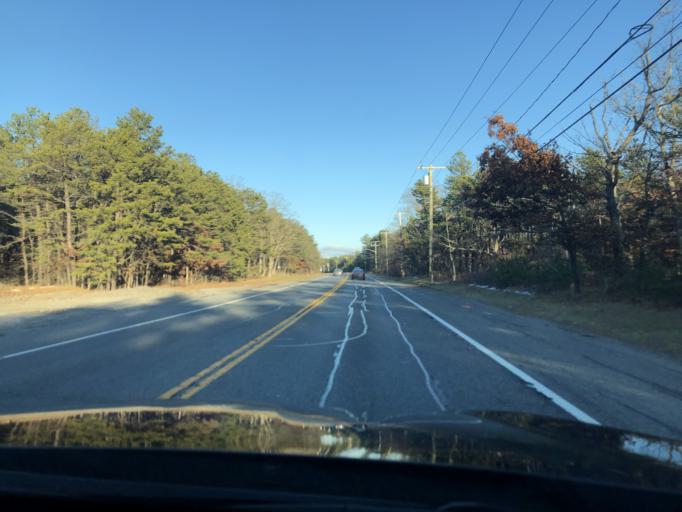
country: US
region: New York
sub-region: Suffolk County
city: Wading River
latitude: 40.9065
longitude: -72.8508
